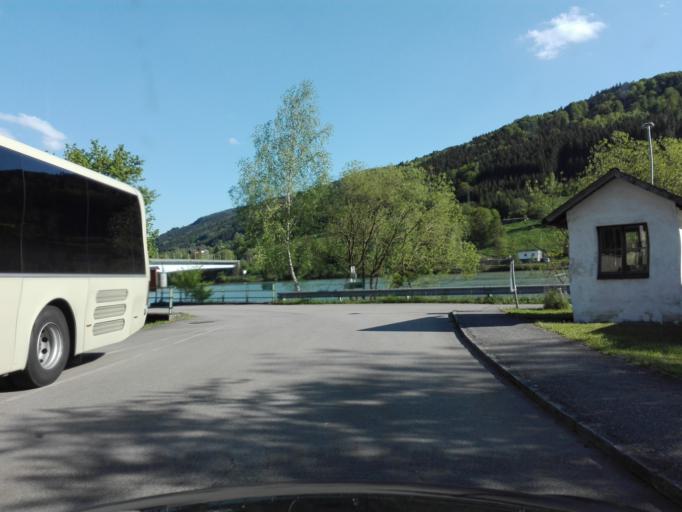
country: AT
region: Upper Austria
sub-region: Politischer Bezirk Rohrbach
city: Pfarrkirchen im Muehlkreis
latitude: 48.4677
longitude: 13.7924
